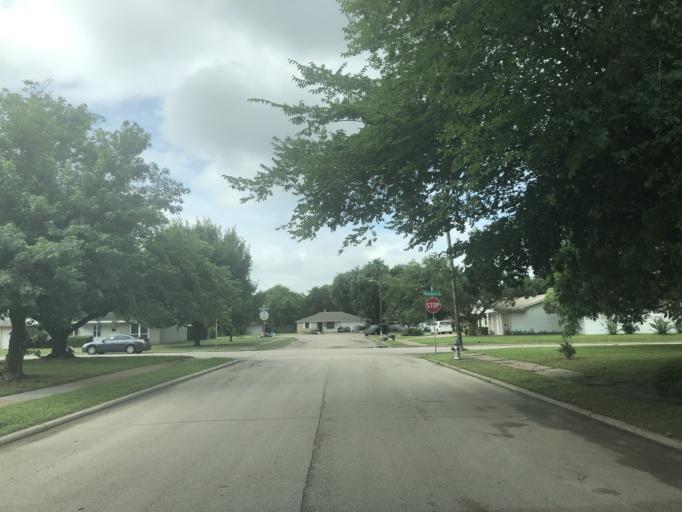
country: US
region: Texas
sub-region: Dallas County
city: Irving
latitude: 32.8052
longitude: -96.9864
